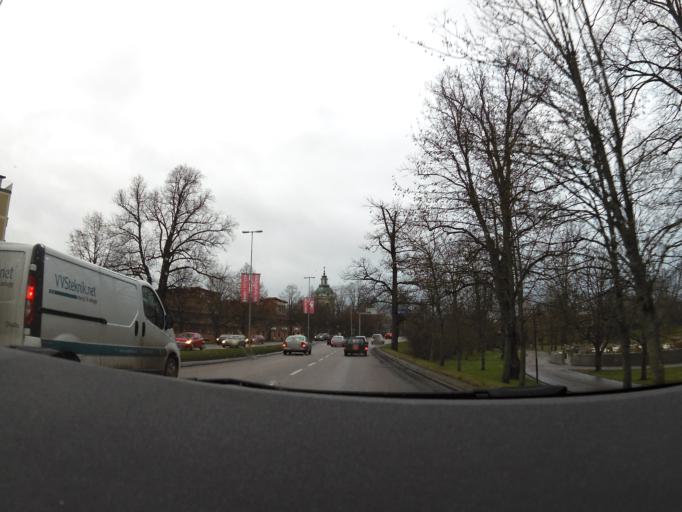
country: SE
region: Gaevleborg
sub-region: Gavle Kommun
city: Gavle
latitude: 60.6741
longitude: 17.1323
